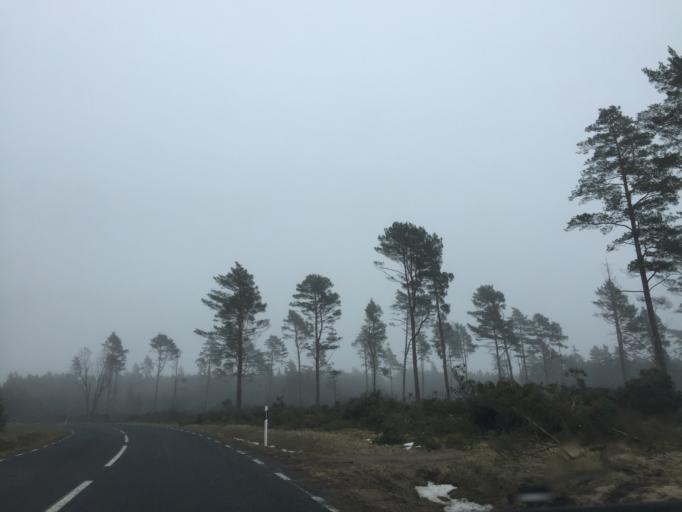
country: EE
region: Saare
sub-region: Kuressaare linn
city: Kuressaare
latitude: 58.4676
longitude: 22.0210
